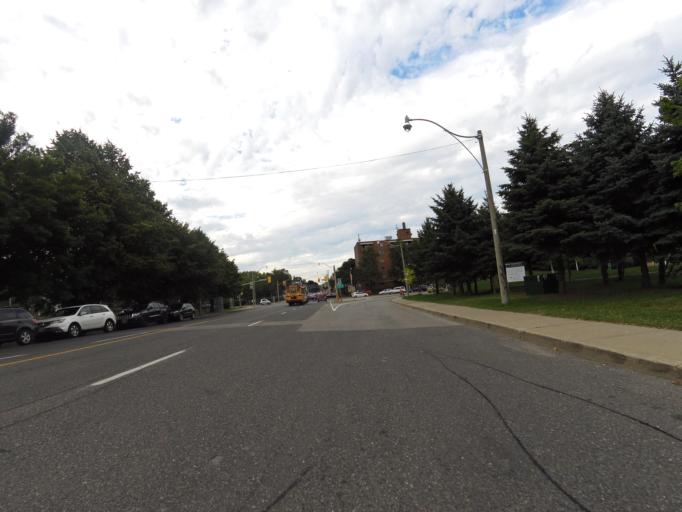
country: CA
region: Ontario
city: Toronto
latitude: 43.6647
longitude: -79.3158
